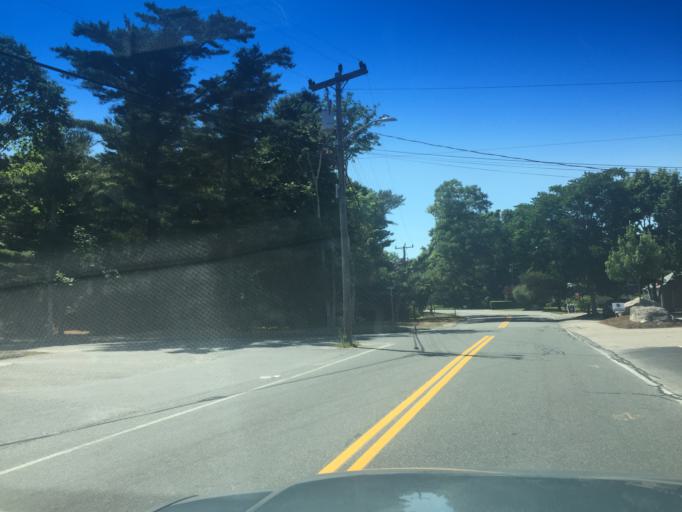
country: US
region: Massachusetts
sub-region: Barnstable County
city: Pocasset
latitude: 41.6934
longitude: -70.6197
